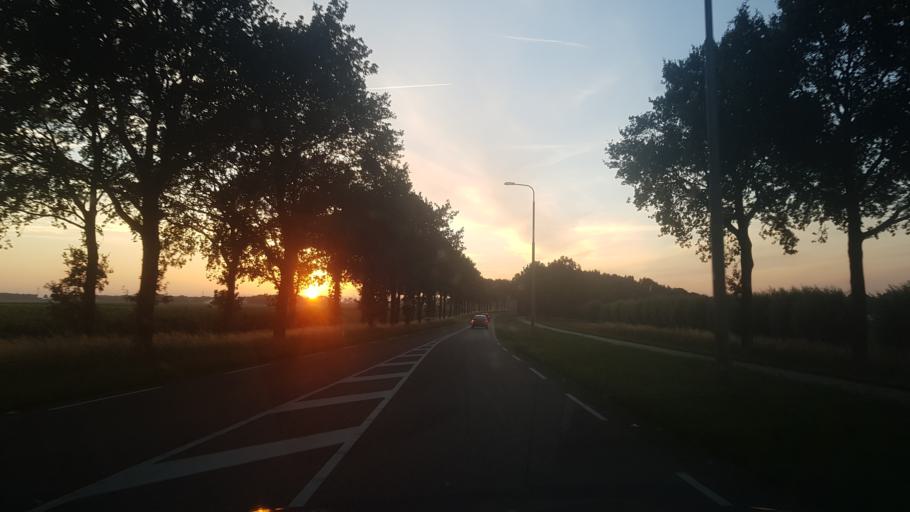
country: NL
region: Flevoland
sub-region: Gemeente Noordoostpolder
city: Emmeloord
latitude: 52.6987
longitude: 5.7243
